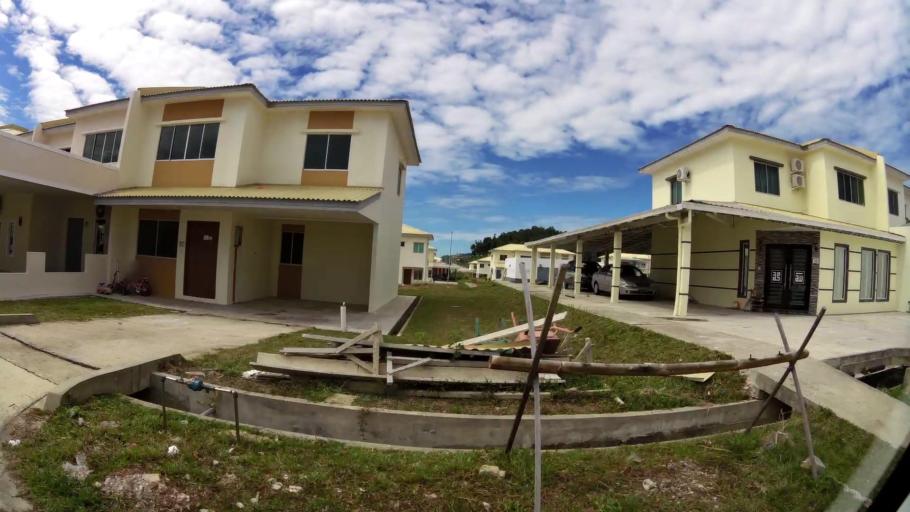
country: BN
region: Brunei and Muara
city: Bandar Seri Begawan
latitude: 4.9898
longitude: 115.0091
